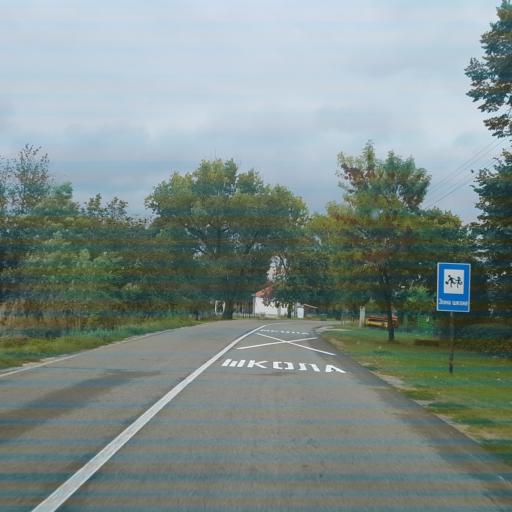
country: RS
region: Central Serbia
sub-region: Nisavski Okrug
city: Aleksinac
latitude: 43.5975
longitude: 21.6234
